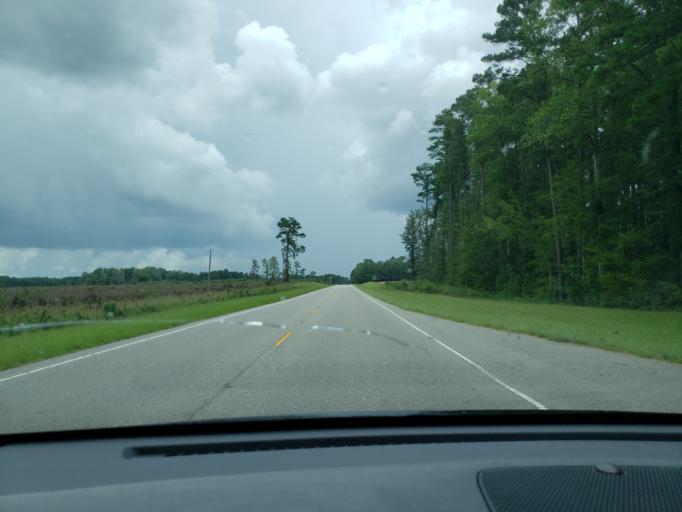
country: US
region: North Carolina
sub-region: Bladen County
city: Bladenboro
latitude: 34.4748
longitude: -78.6677
